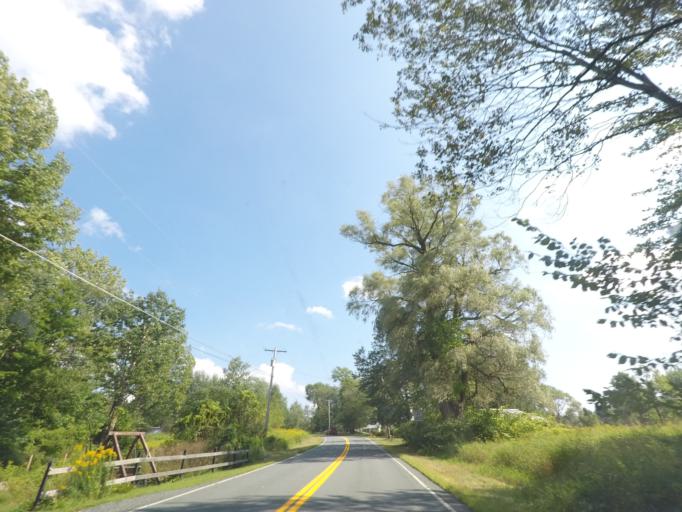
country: US
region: New York
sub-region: Rensselaer County
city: Poestenkill
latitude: 42.6836
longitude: -73.5233
